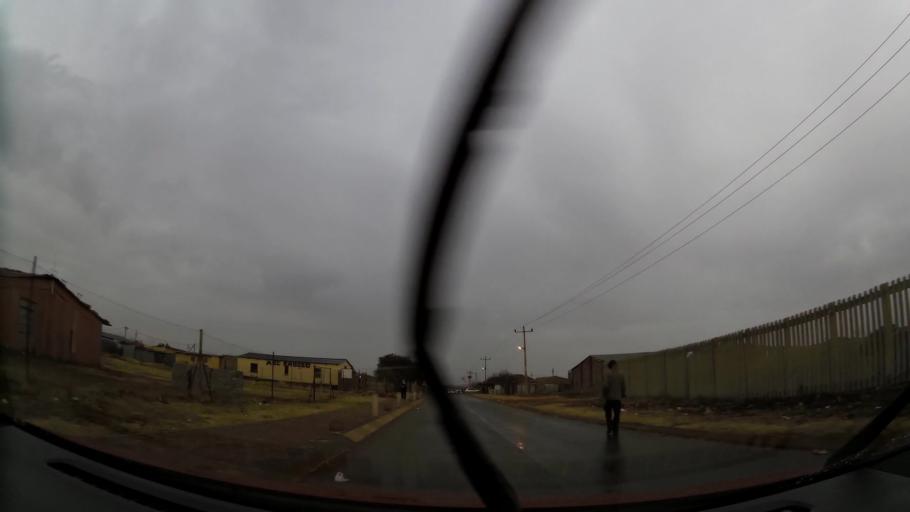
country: ZA
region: Gauteng
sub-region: West Rand District Municipality
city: Randfontein
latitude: -26.1754
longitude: 27.7845
